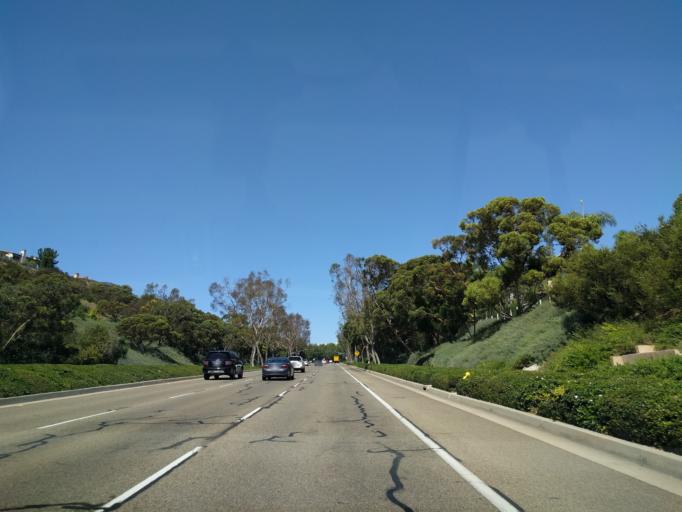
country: US
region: California
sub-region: Orange County
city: San Joaquin Hills
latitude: 33.5928
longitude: -117.8352
